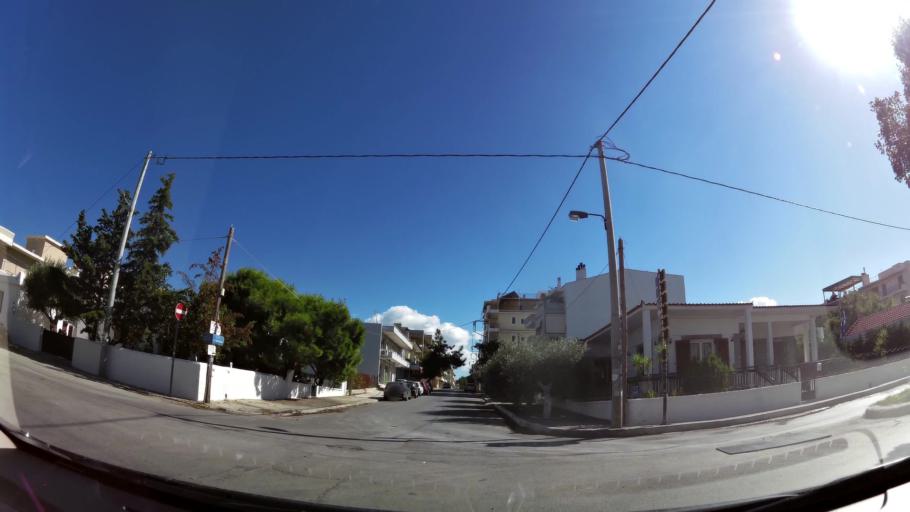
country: GR
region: Attica
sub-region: Nomarchia Anatolikis Attikis
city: Markopoulo
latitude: 37.8883
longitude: 23.9299
